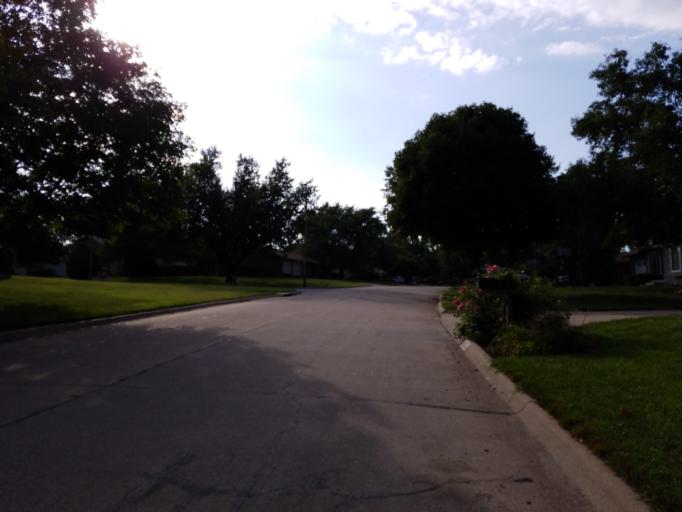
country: US
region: Kansas
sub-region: Riley County
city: Manhattan
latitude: 39.2069
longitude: -96.6210
